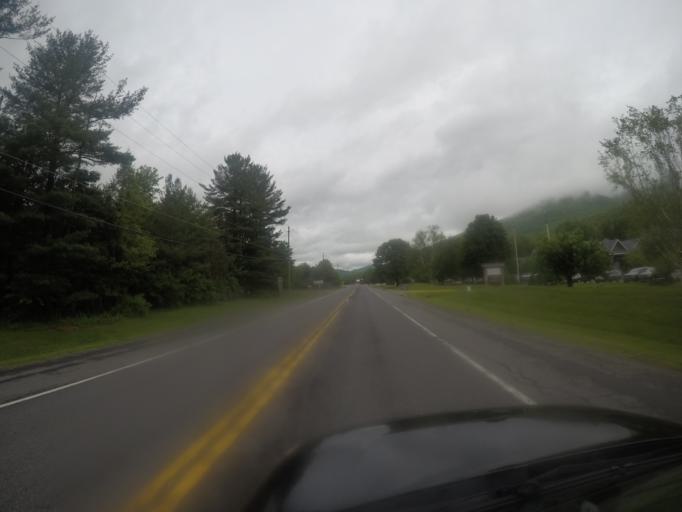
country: US
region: New York
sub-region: Ulster County
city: Shokan
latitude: 42.0490
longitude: -74.2877
